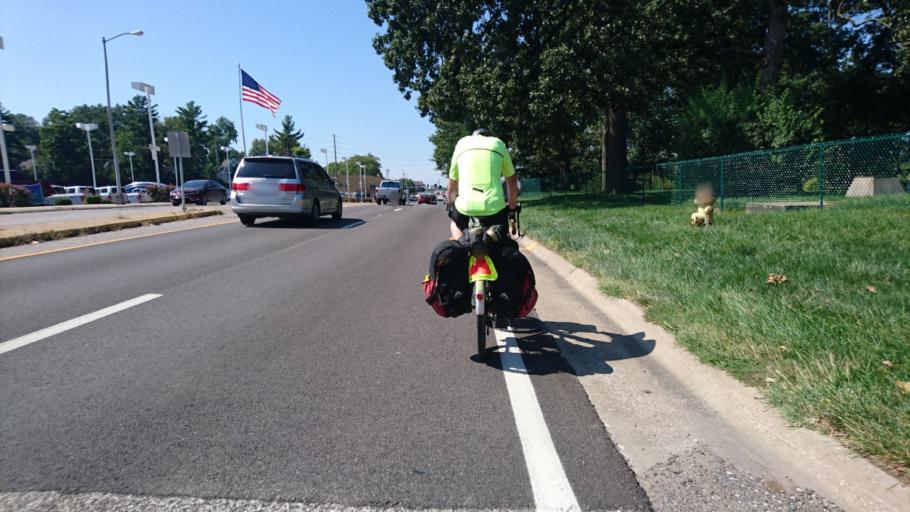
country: US
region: Missouri
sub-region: Saint Louis County
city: Warson Woods
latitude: 38.6008
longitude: -90.3983
